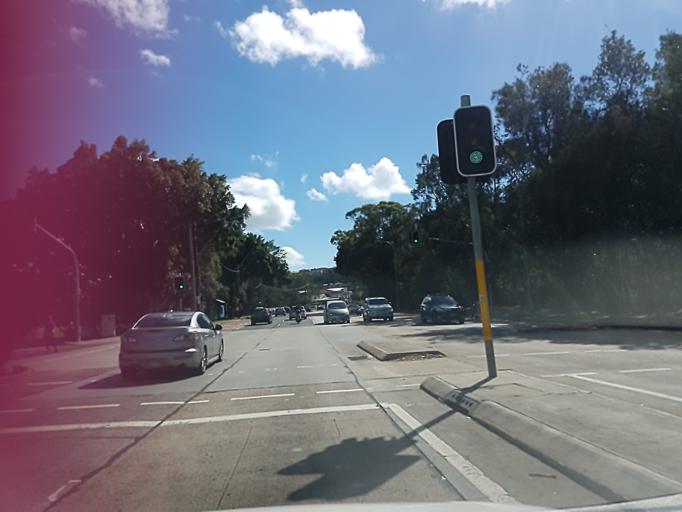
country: AU
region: New South Wales
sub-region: Warringah
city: Dee Why
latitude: -33.7480
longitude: 151.2905
